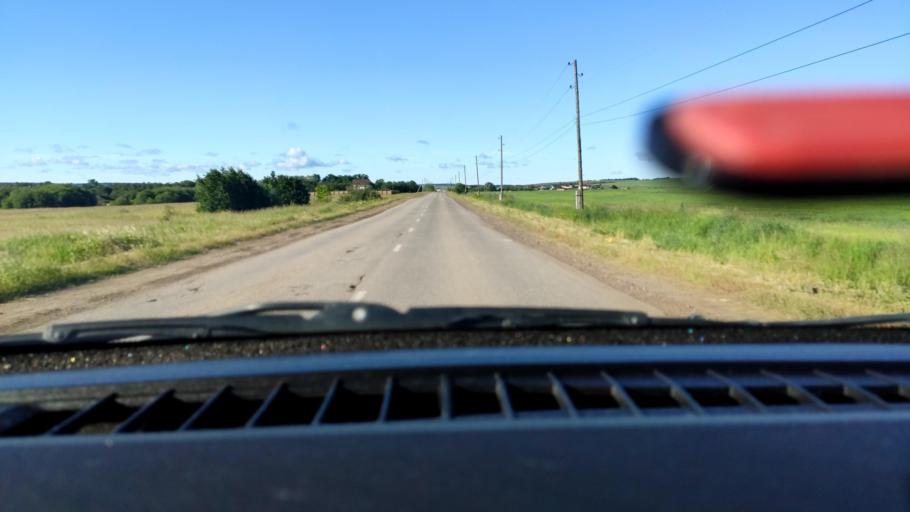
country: RU
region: Perm
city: Kultayevo
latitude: 57.8813
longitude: 55.9225
